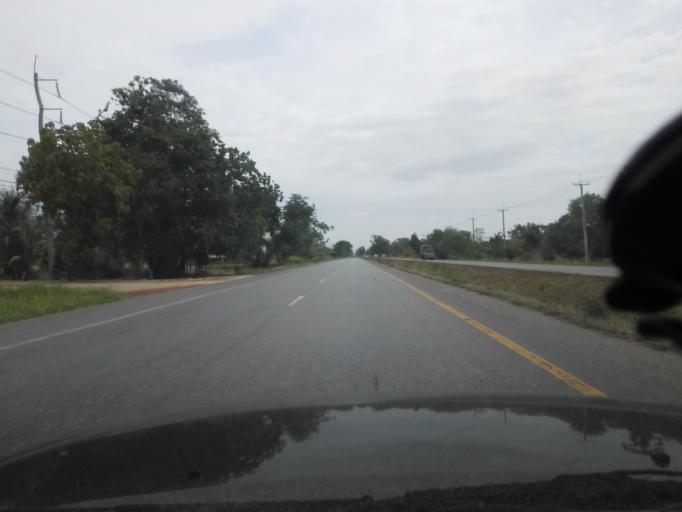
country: TH
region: Kamphaeng Phet
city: Khlong Khlung
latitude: 16.1105
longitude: 99.7191
